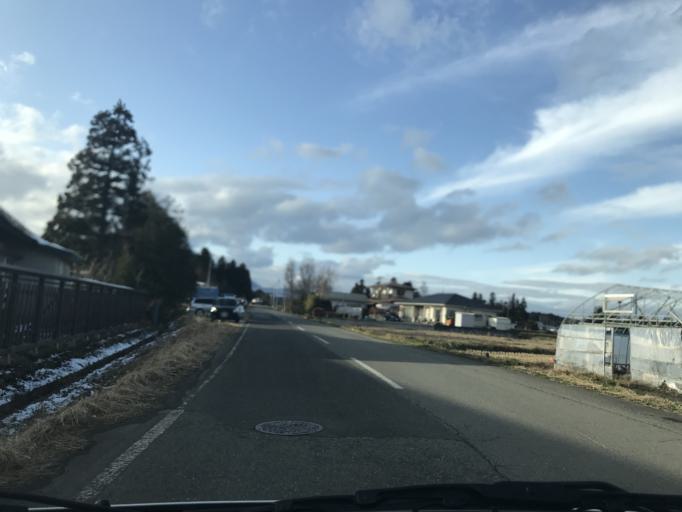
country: JP
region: Iwate
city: Mizusawa
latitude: 39.1886
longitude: 141.0957
